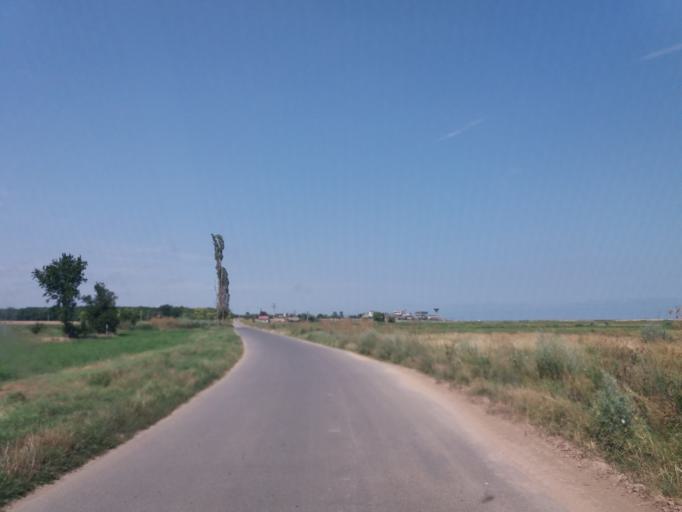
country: RO
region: Constanta
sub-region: Comuna Sacele
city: Sacele
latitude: 44.4391
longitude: 28.7272
